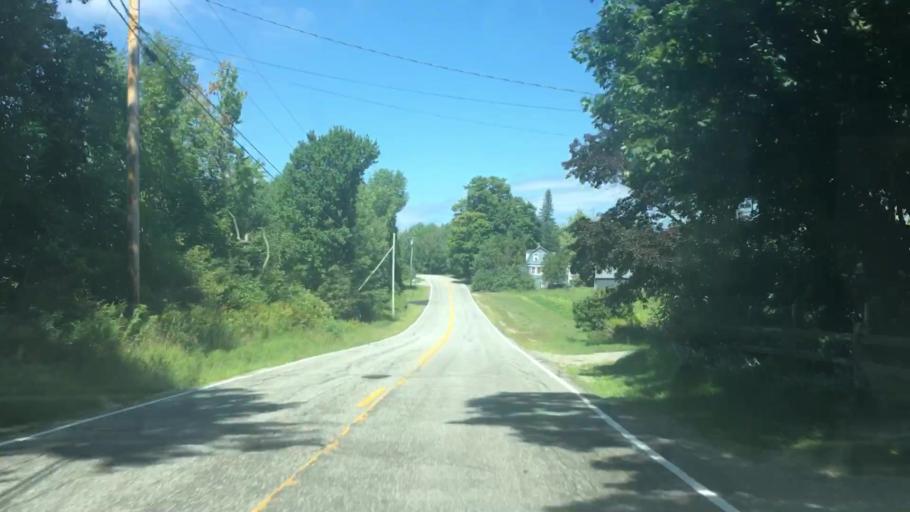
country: US
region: Maine
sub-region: Kennebec County
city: Monmouth
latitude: 44.1846
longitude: -69.9391
